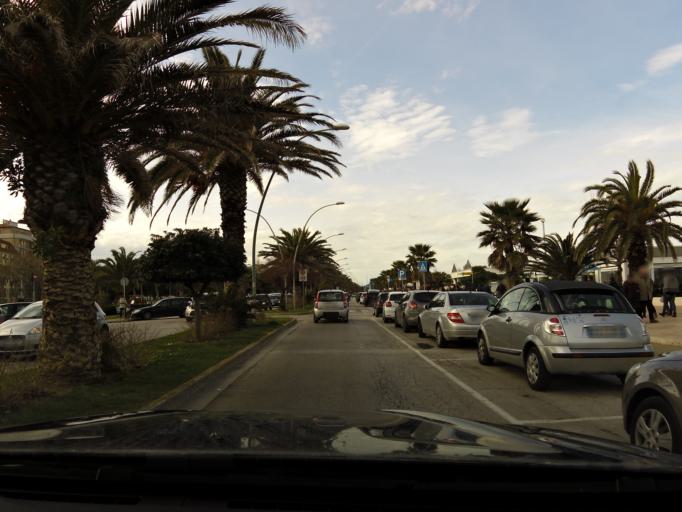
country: IT
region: The Marches
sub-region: Provincia di Macerata
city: Portocivitanova
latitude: 43.3048
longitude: 13.7354
